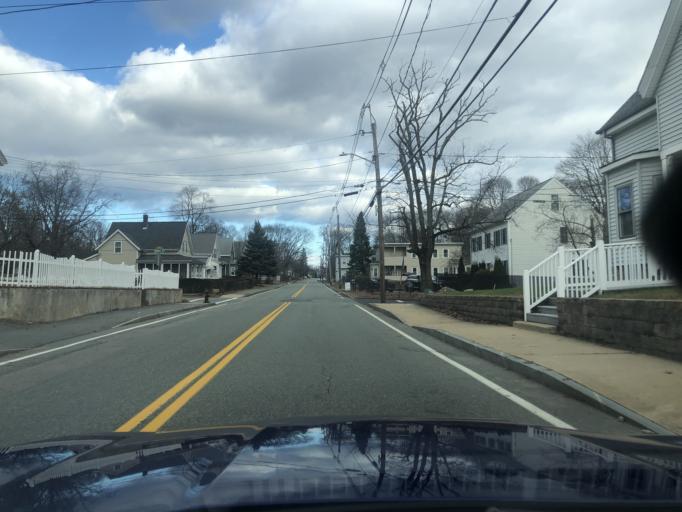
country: US
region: Massachusetts
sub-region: Plymouth County
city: Brockton
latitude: 42.1110
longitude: -71.0169
